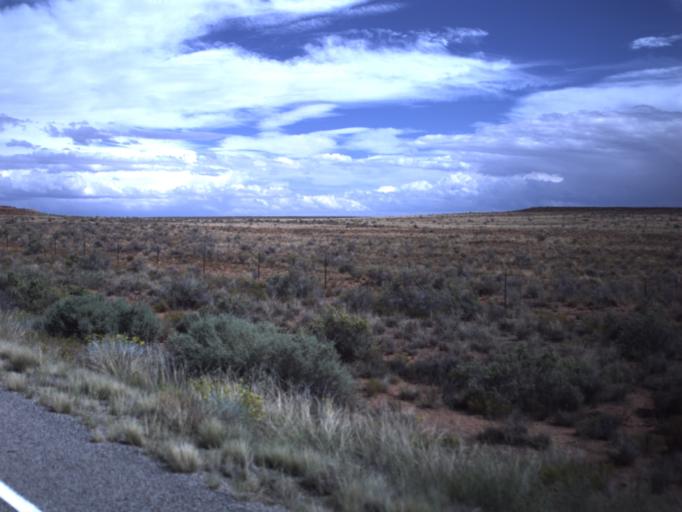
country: US
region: Utah
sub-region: San Juan County
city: Blanding
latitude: 37.2572
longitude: -109.7434
